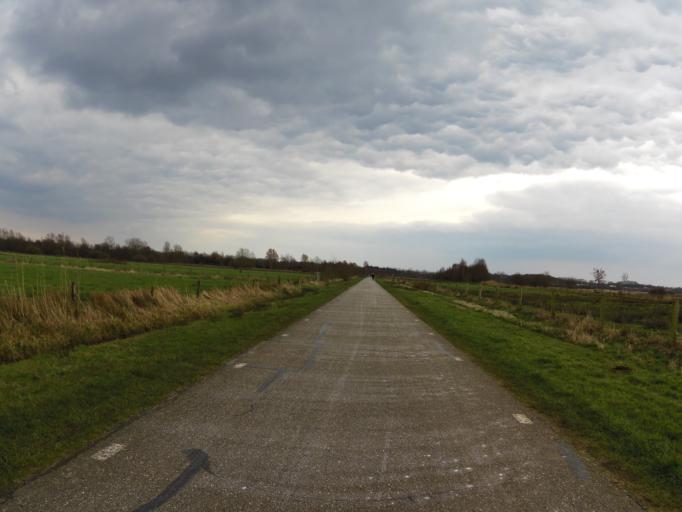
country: NL
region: North Brabant
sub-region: Gemeente 's-Hertogenbosch
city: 's-Hertogenbosch
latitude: 51.6775
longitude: 5.3059
